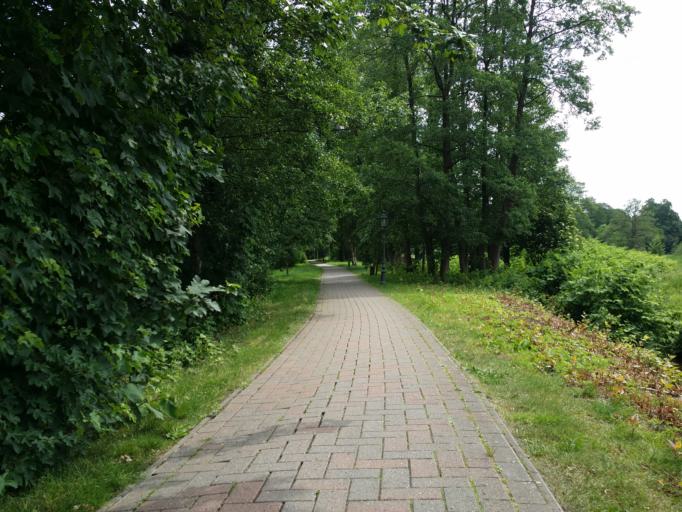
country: DE
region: Lower Saxony
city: Zetel
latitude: 53.3885
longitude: 7.9486
